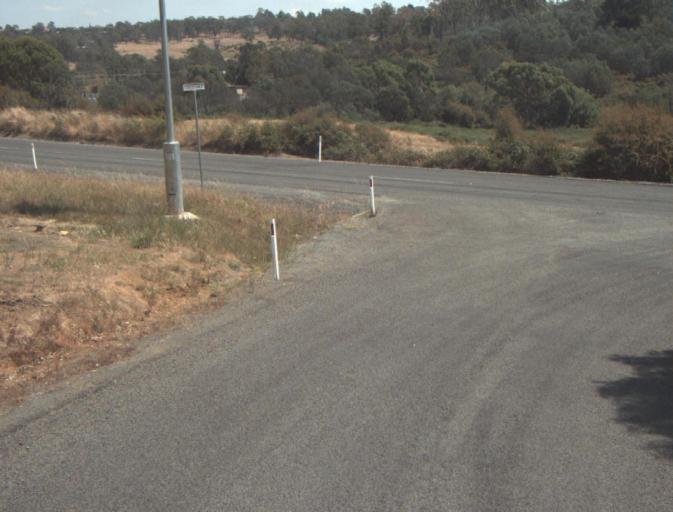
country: AU
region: Tasmania
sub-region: Launceston
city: Newstead
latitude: -41.4715
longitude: 147.1887
